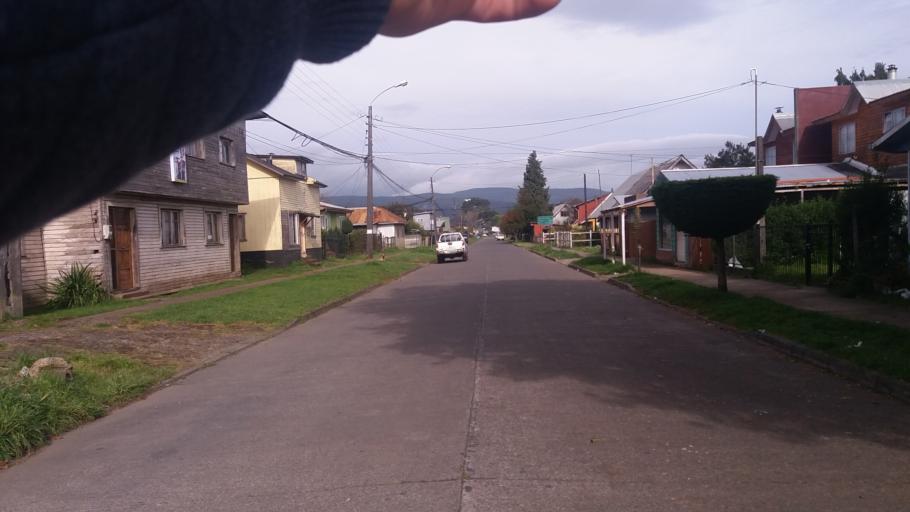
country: CL
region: Araucania
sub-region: Provincia de Cautin
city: Carahue
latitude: -39.1784
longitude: -73.1690
